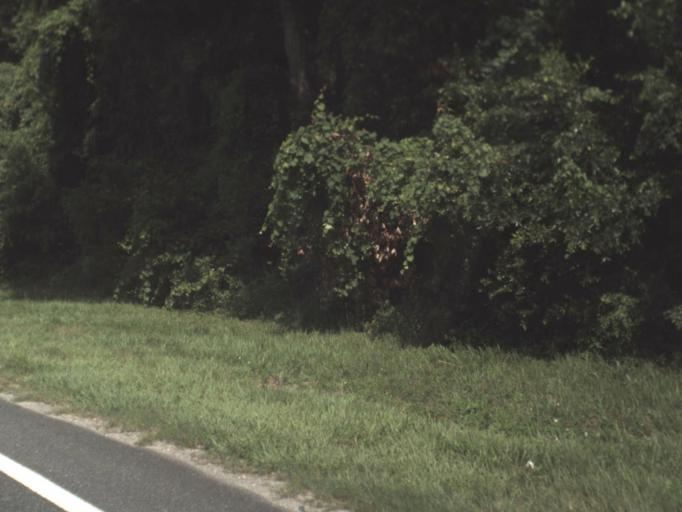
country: US
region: Florida
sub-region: Alachua County
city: Archer
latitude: 29.5910
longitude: -82.4365
